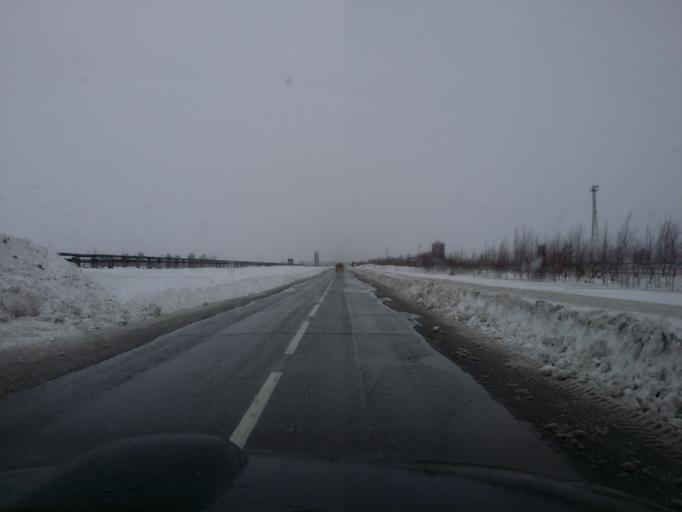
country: RU
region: Khanty-Mansiyskiy Avtonomnyy Okrug
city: Izluchinsk
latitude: 60.9764
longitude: 76.9301
